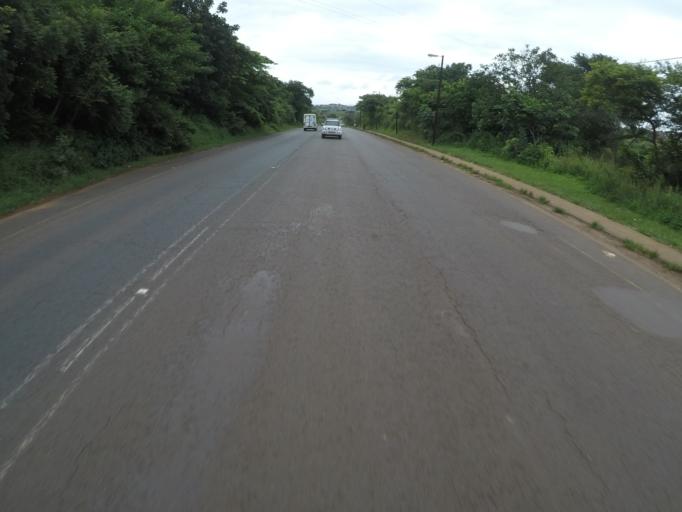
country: ZA
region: KwaZulu-Natal
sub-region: uThungulu District Municipality
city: Empangeni
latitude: -28.7764
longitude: 31.8854
